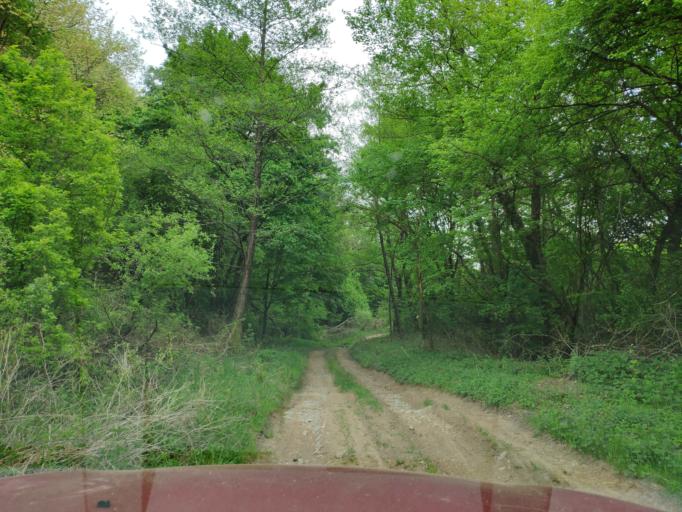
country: SK
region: Banskobystricky
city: Revuca
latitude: 48.5186
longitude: 20.1613
